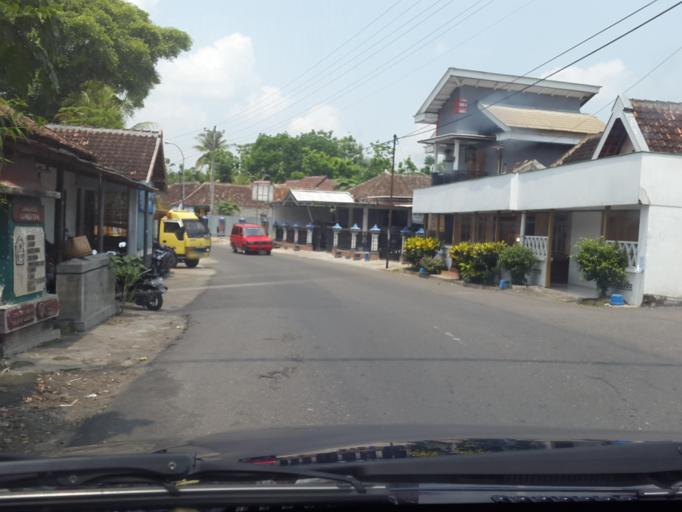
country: ID
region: Daerah Istimewa Yogyakarta
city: Wonosari
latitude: -7.9705
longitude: 110.5898
